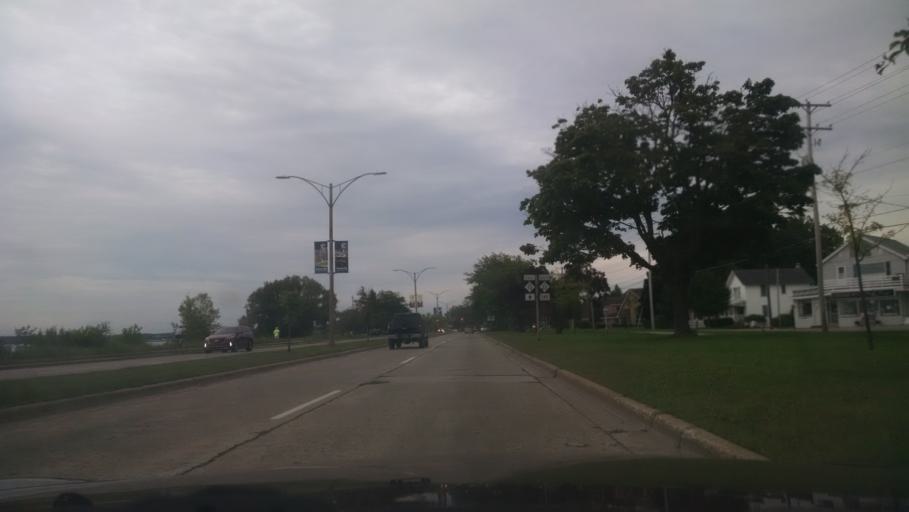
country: US
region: Michigan
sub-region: Leelanau County
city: Greilickville
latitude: 44.7705
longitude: -85.6368
